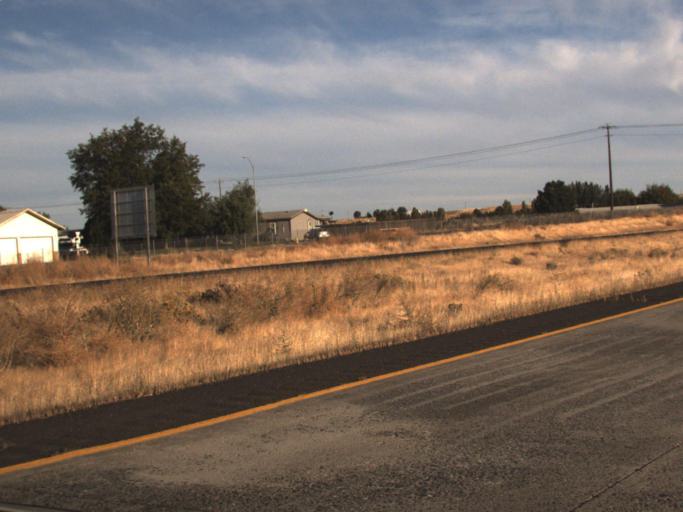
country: US
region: Washington
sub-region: Franklin County
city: Connell
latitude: 46.6589
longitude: -118.8512
